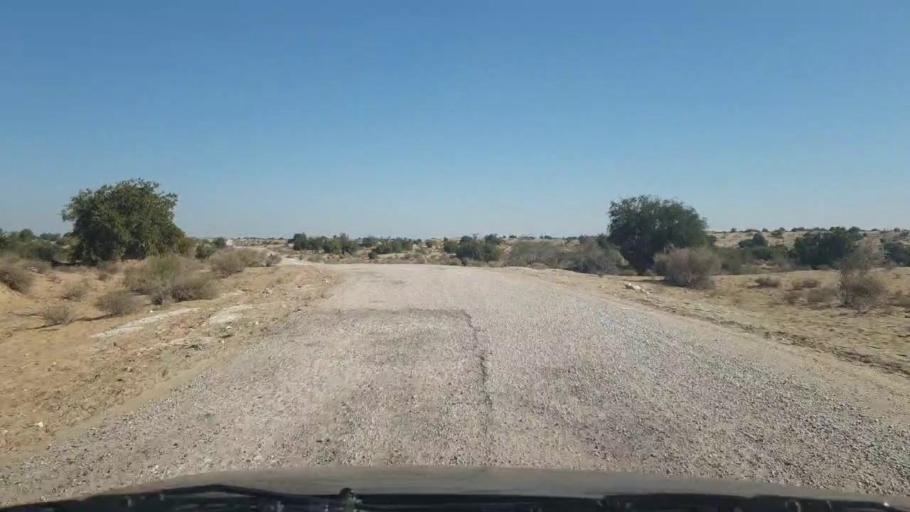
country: PK
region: Sindh
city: Bozdar
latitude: 27.0032
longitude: 68.8842
